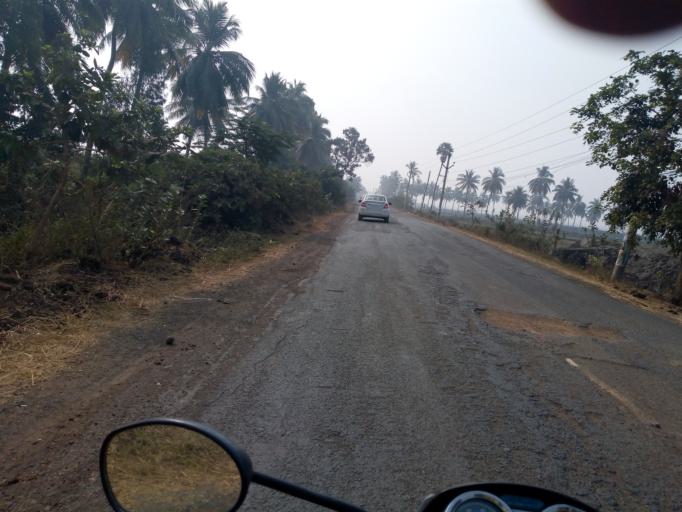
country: IN
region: Andhra Pradesh
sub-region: West Godavari
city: Tadepallegudem
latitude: 16.7420
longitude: 81.4193
